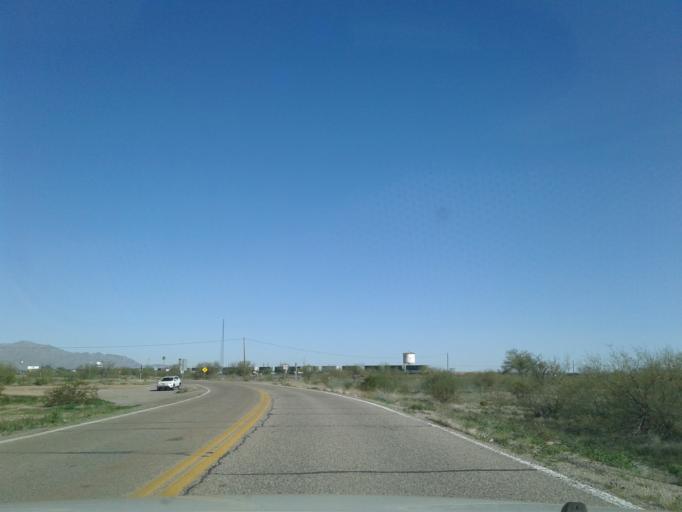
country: US
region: Arizona
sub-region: Pima County
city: Avra Valley
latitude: 32.5732
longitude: -111.3253
